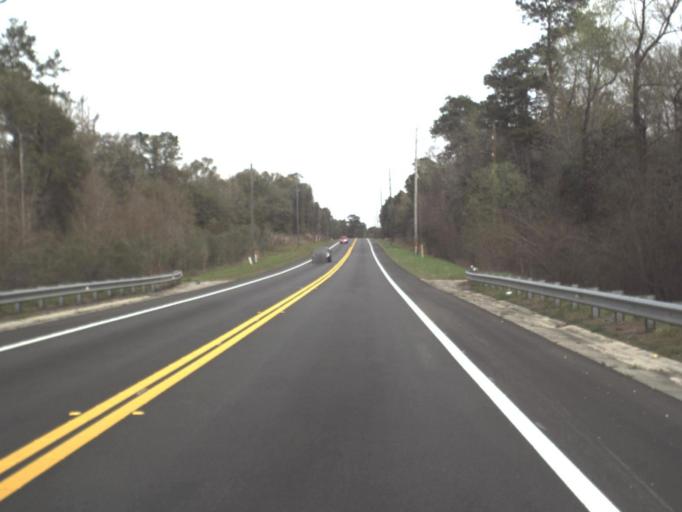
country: US
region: Florida
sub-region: Gadsden County
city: Midway
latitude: 30.4011
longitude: -84.5931
